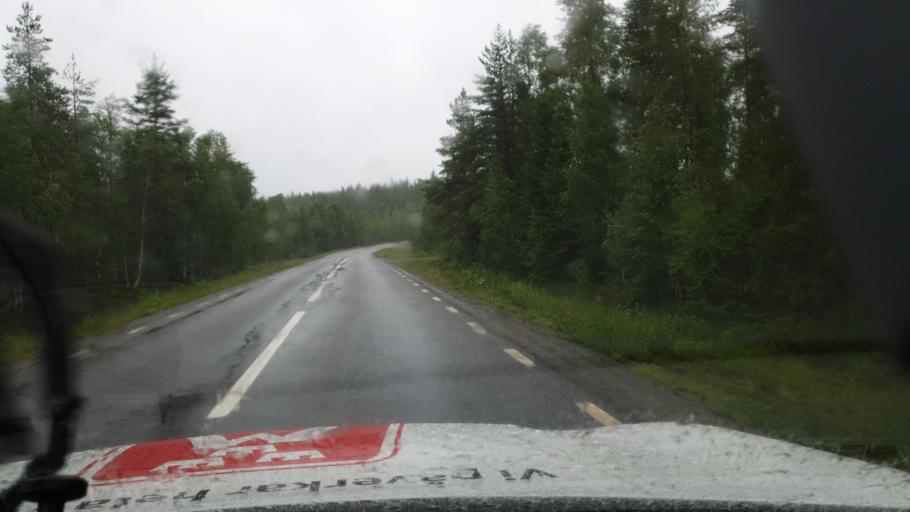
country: SE
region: Vaesterbotten
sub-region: Skelleftea Kommun
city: Burtraesk
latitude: 64.3371
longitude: 20.2341
